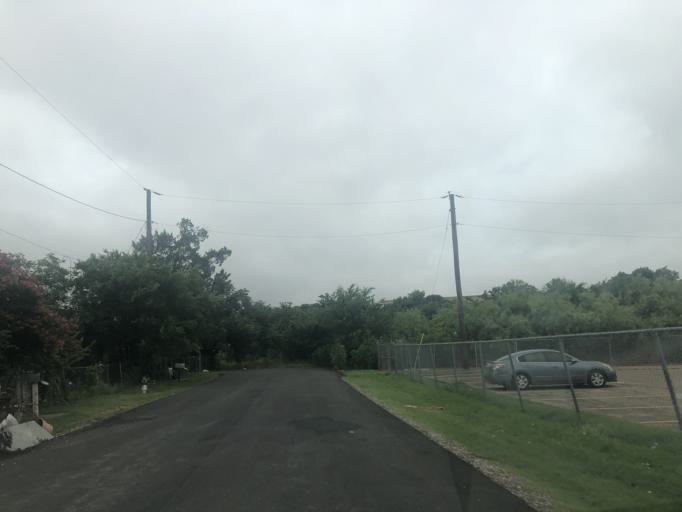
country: US
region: Texas
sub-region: Dallas County
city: Cockrell Hill
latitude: 32.7771
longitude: -96.8673
